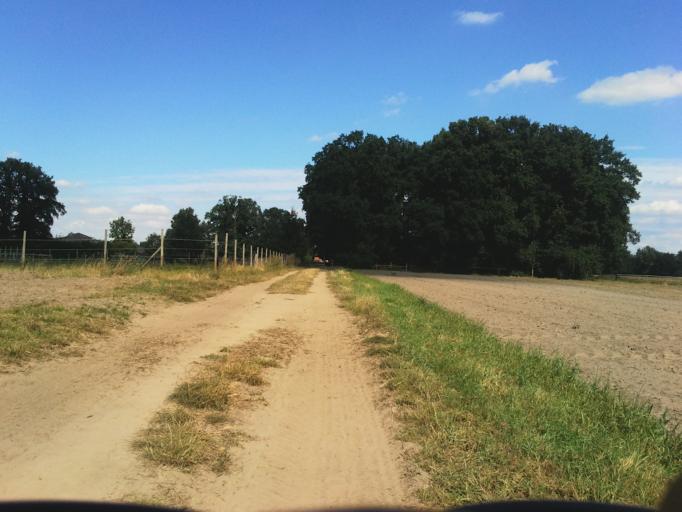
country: DE
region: Lower Saxony
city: Nienburg
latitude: 52.6564
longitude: 9.2397
